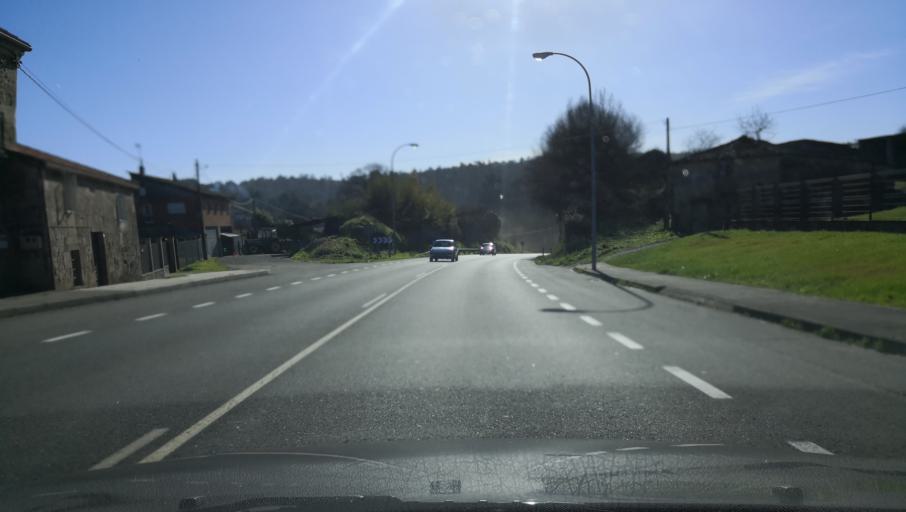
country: ES
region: Galicia
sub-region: Provincia de Pontevedra
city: Silleda
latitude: 42.7347
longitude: -8.3212
